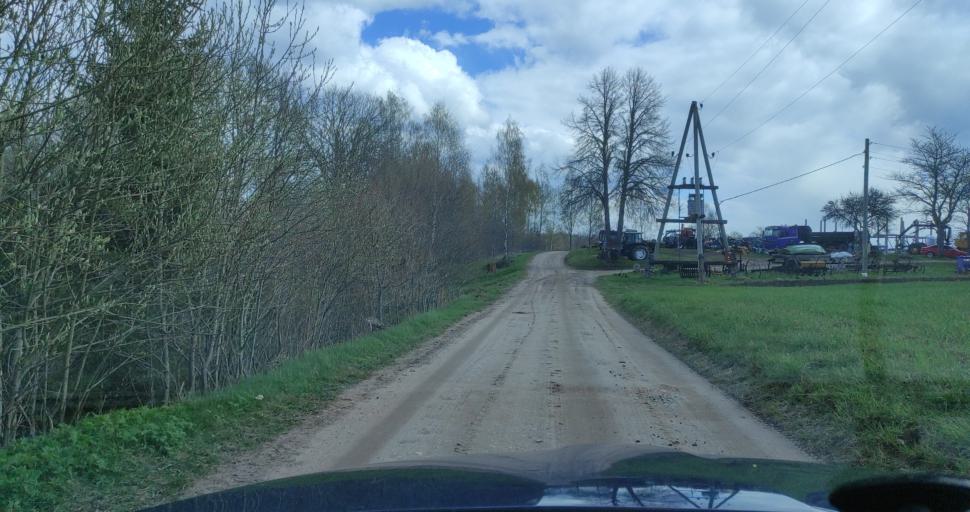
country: LV
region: Kuldigas Rajons
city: Kuldiga
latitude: 56.8602
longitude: 21.8355
